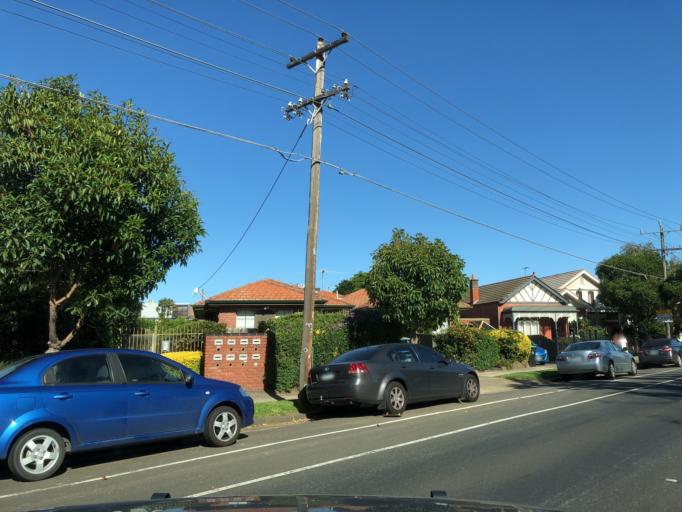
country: AU
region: Victoria
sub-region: Moonee Valley
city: Moonee Ponds
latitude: -37.7616
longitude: 144.9215
